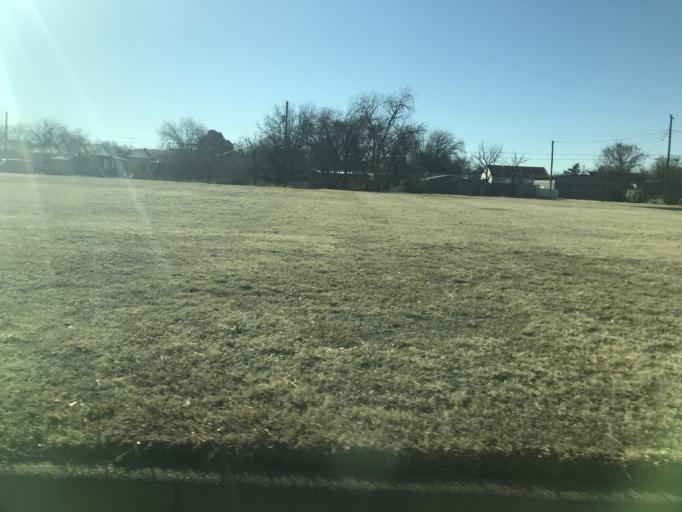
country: US
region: Texas
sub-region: Taylor County
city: Abilene
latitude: 32.4396
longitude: -99.7577
